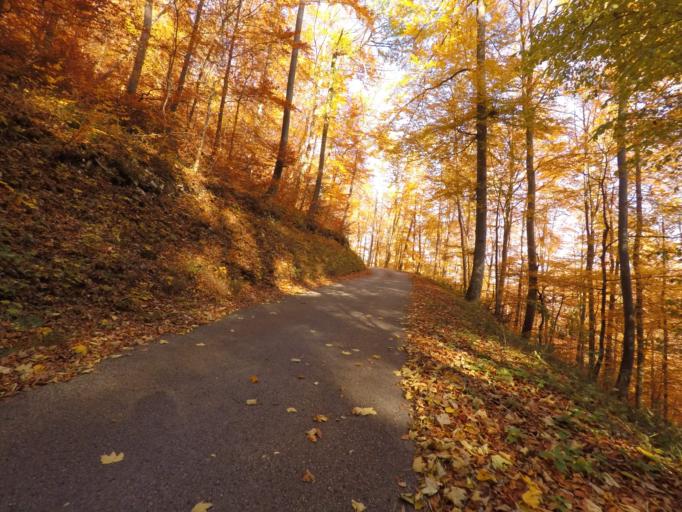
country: DE
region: Baden-Wuerttemberg
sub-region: Tuebingen Region
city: Pfullingen
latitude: 48.4405
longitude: 9.2316
